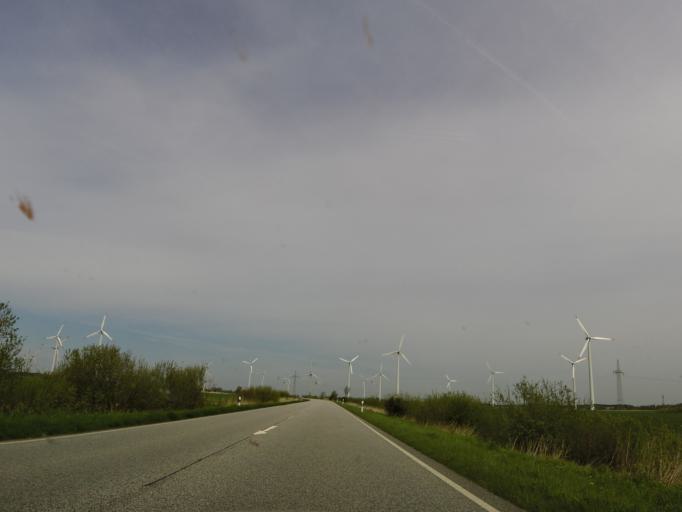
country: DE
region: Schleswig-Holstein
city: Stelle-Wittenwurth
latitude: 54.2570
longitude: 9.0363
